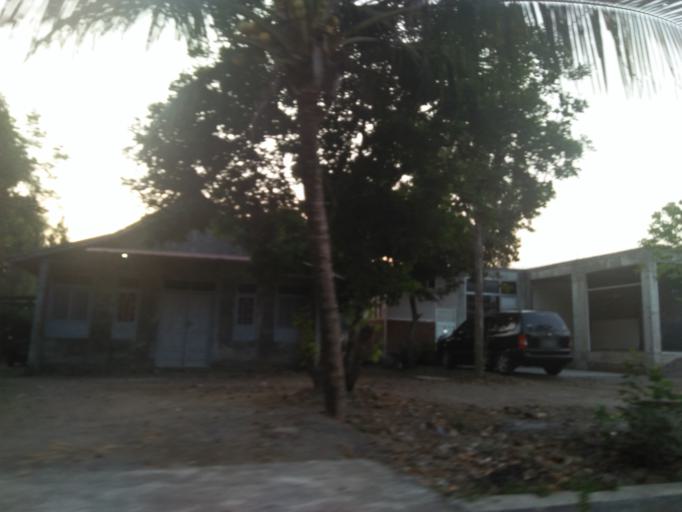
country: ID
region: Daerah Istimewa Yogyakarta
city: Sewon
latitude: -7.8537
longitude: 110.4098
